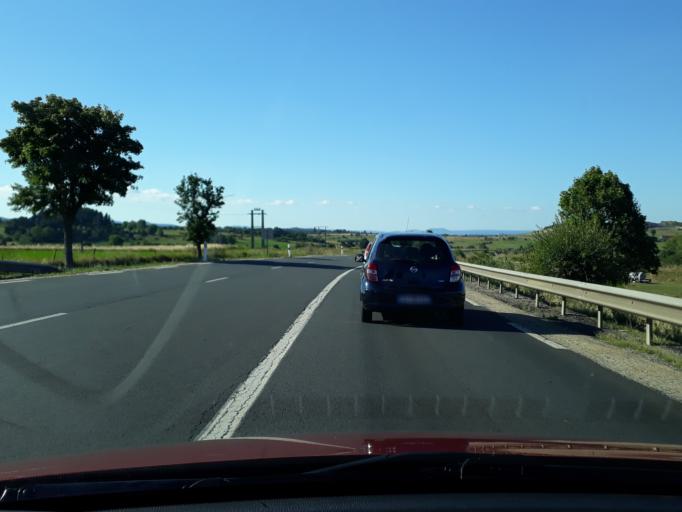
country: FR
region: Auvergne
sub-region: Departement de la Haute-Loire
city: Solignac-sur-Loire
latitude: 44.9173
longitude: 3.8452
